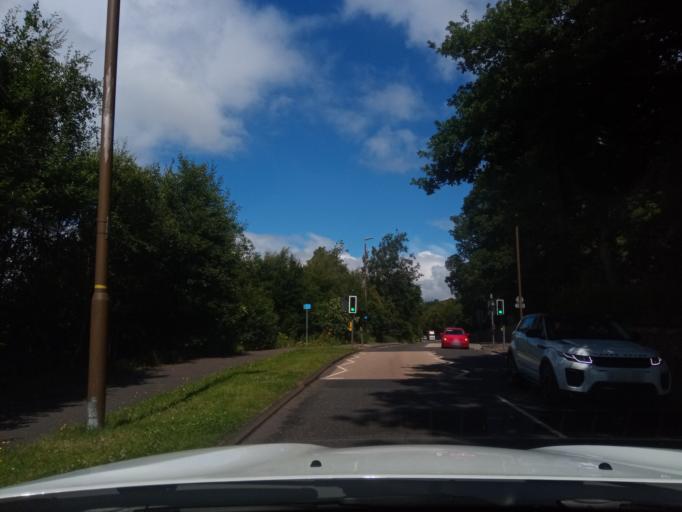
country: GB
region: Scotland
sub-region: Stirling
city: Bridge of Allan
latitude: 56.1409
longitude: -3.9263
